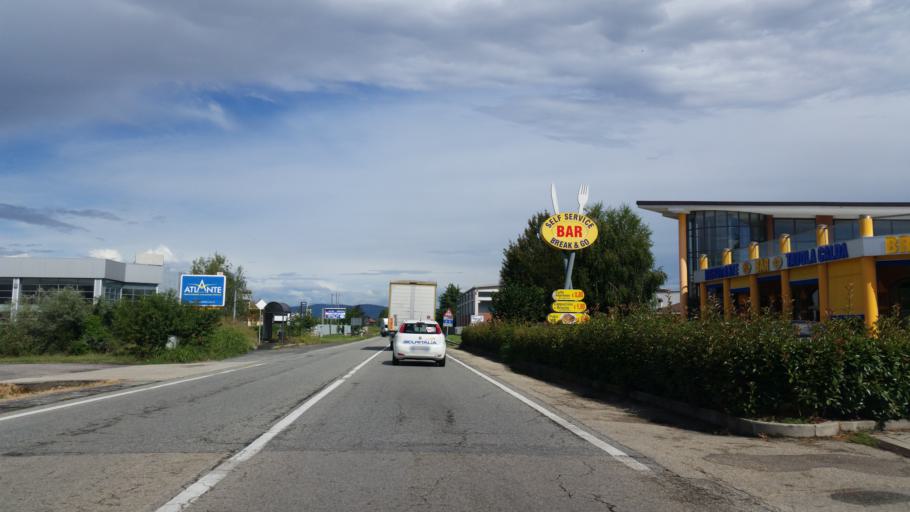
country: IT
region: Piedmont
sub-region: Provincia di Torino
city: Poirino
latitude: 44.9288
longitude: 7.8346
